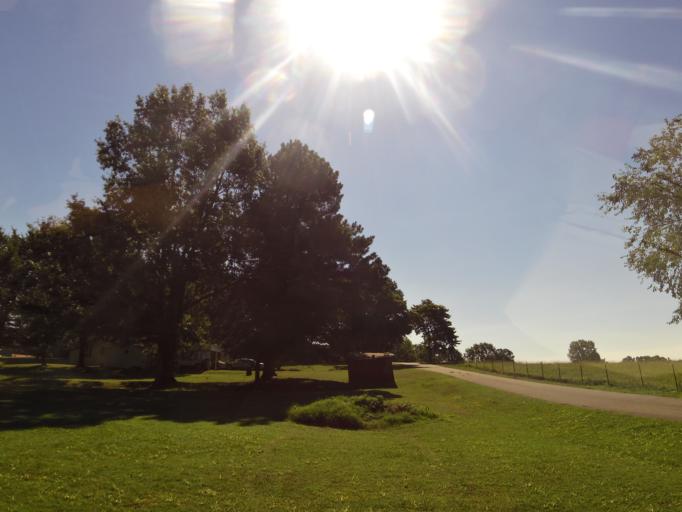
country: US
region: Arkansas
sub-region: Clay County
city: Piggott
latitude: 36.4275
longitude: -90.2715
